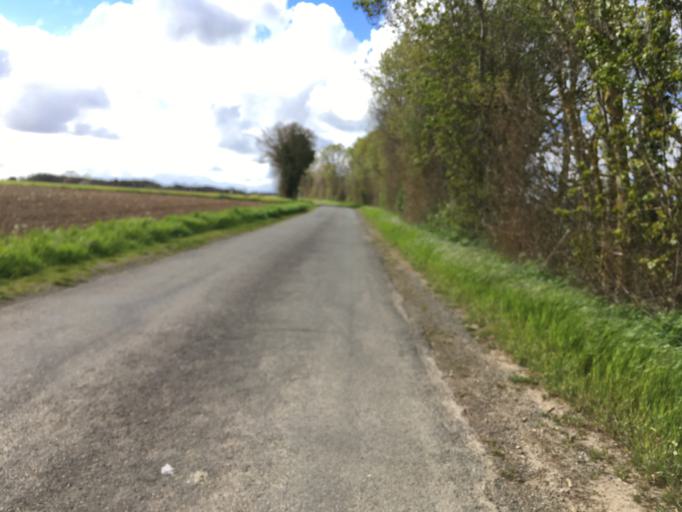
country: FR
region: Poitou-Charentes
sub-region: Departement de la Charente-Maritime
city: Le Thou
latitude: 46.1292
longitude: -0.8631
